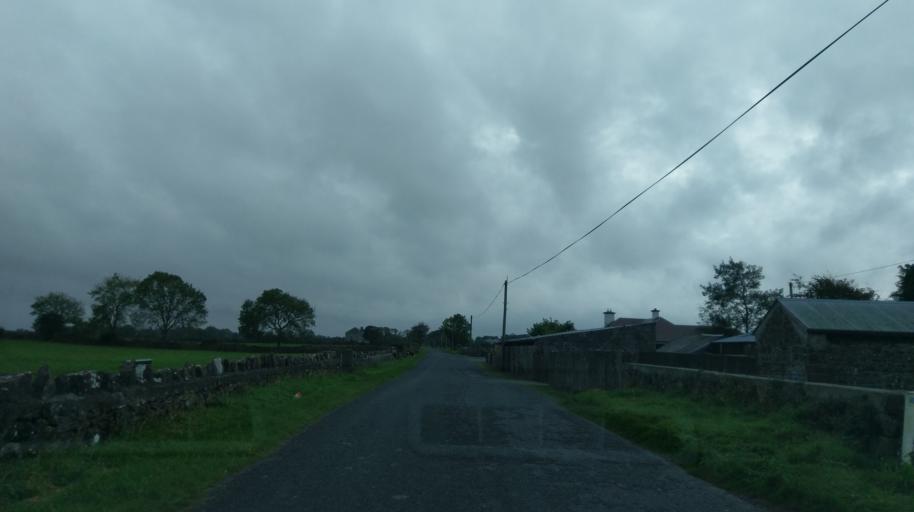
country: IE
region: Connaught
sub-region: County Galway
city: Athenry
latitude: 53.4562
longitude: -8.5998
